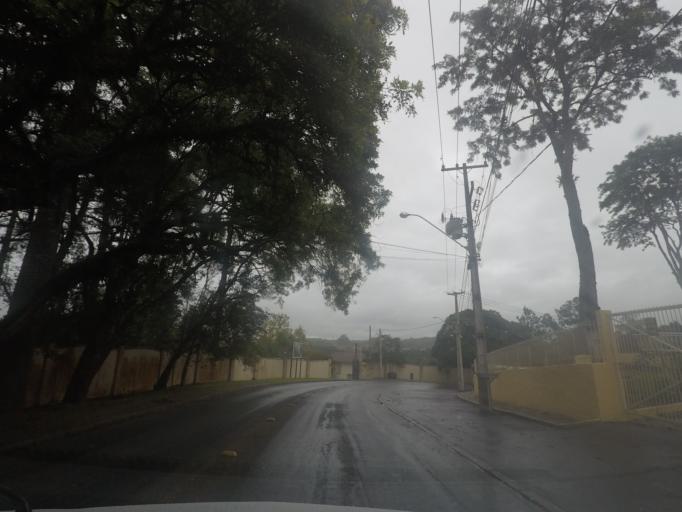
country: BR
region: Parana
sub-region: Quatro Barras
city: Quatro Barras
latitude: -25.3775
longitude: -49.1173
